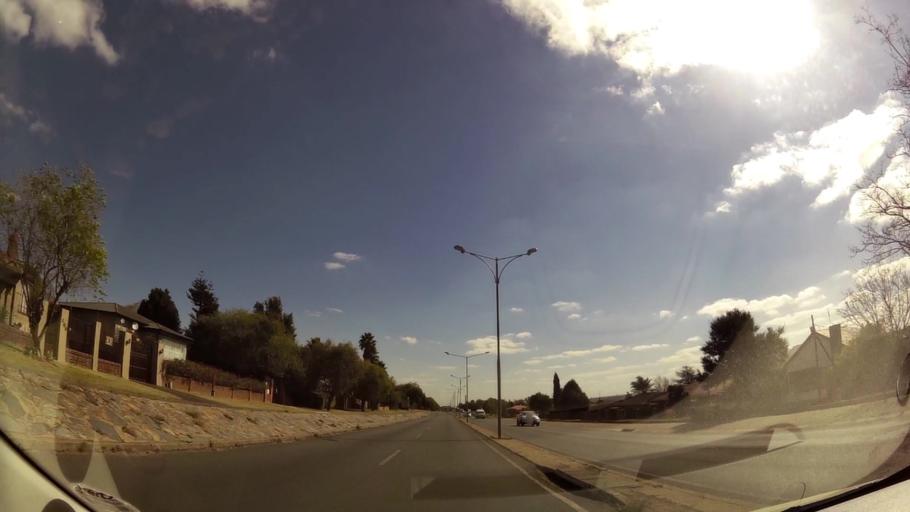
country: ZA
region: Gauteng
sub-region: West Rand District Municipality
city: Krugersdorp
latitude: -26.1124
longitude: 27.7928
